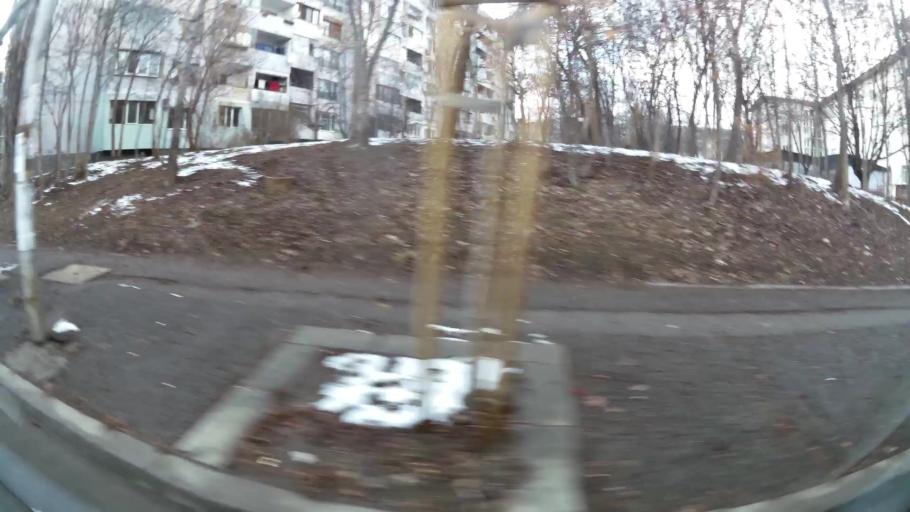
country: BG
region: Sofia-Capital
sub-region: Stolichna Obshtina
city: Sofia
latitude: 42.7077
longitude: 23.2958
